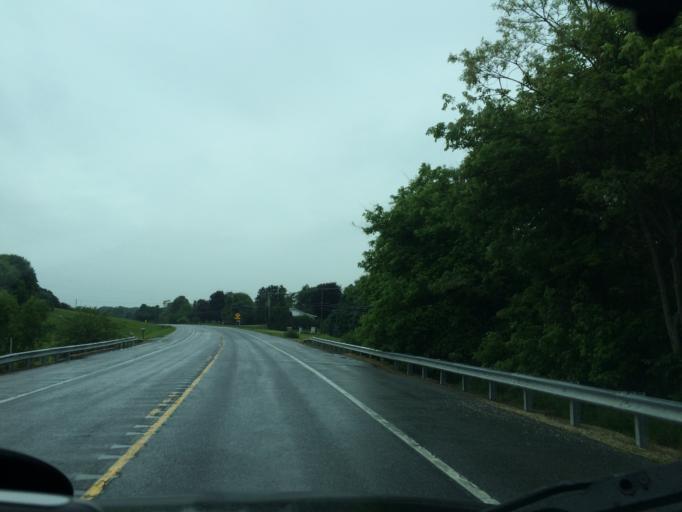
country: US
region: Maryland
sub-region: Washington County
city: Cavetown
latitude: 39.6436
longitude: -77.5925
